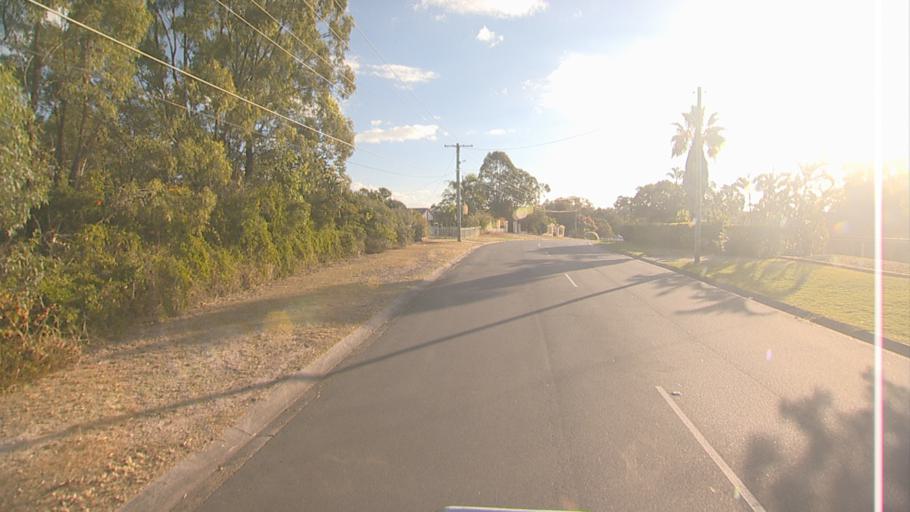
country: AU
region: Queensland
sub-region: Logan
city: Beenleigh
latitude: -27.7086
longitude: 153.1754
